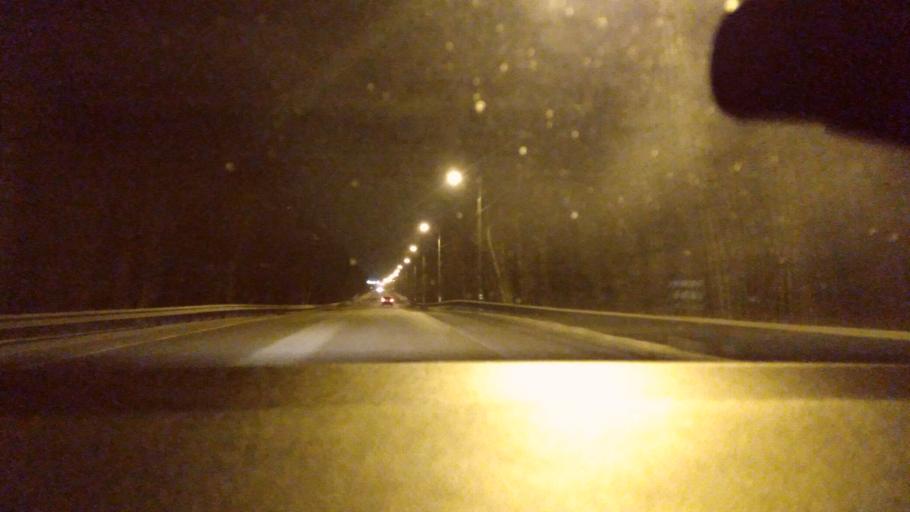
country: RU
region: Moskovskaya
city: Il'inskiy Pogost
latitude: 55.4877
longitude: 38.9028
